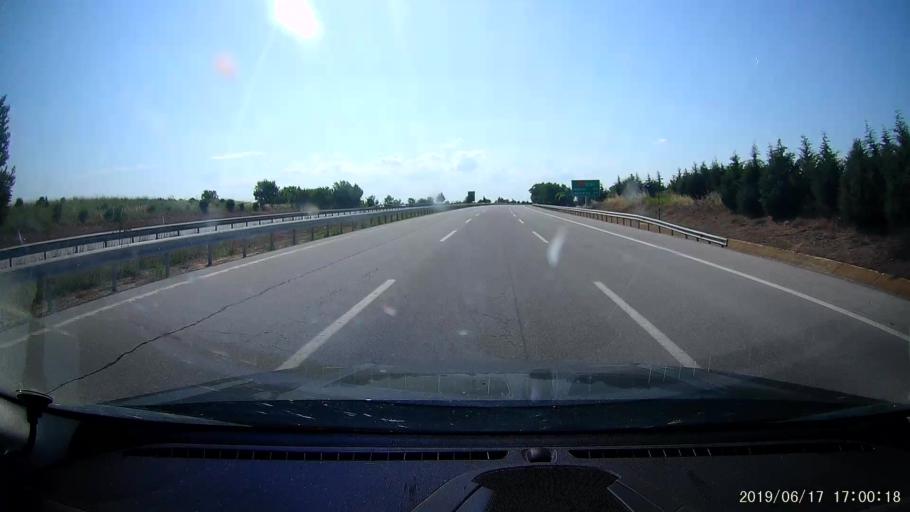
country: TR
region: Edirne
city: Haskoy
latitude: 41.6198
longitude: 26.8351
